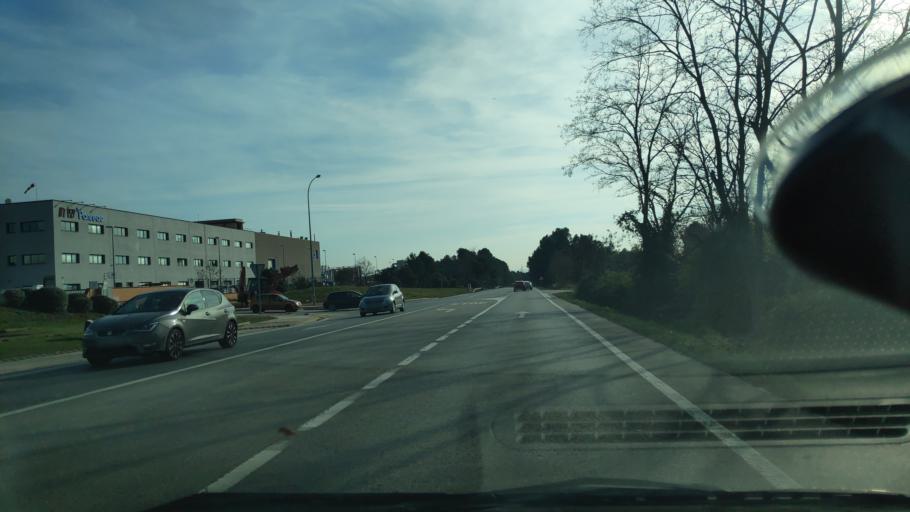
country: ES
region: Catalonia
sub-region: Provincia de Barcelona
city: Castellar del Valles
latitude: 41.5901
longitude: 2.0891
